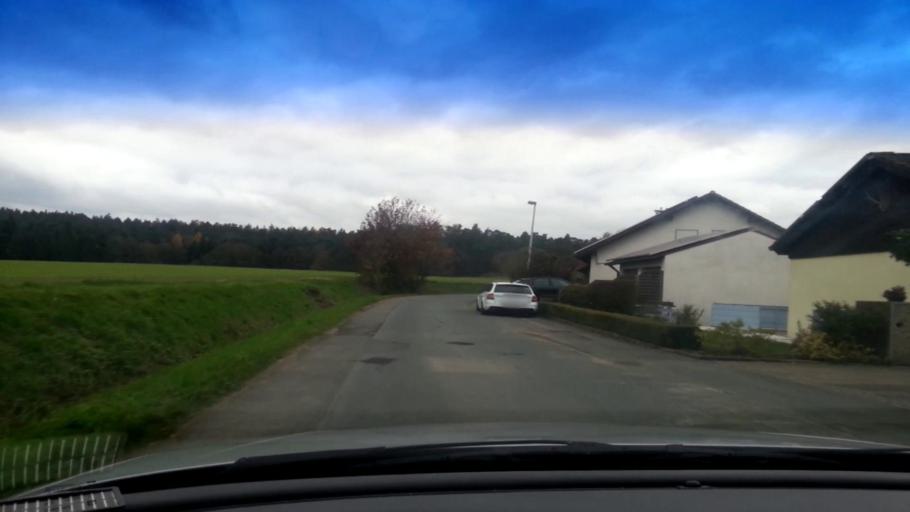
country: DE
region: Bavaria
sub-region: Upper Franconia
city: Stegaurach
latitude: 49.8579
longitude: 10.8264
